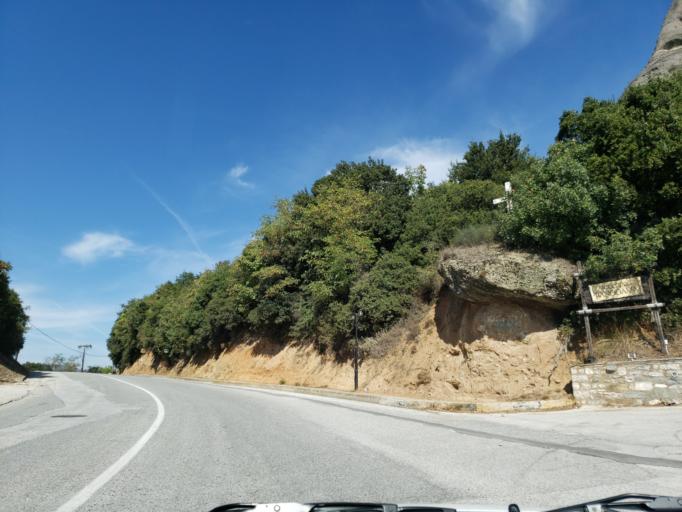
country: GR
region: Thessaly
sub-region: Trikala
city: Kastraki
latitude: 39.7093
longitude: 21.6176
